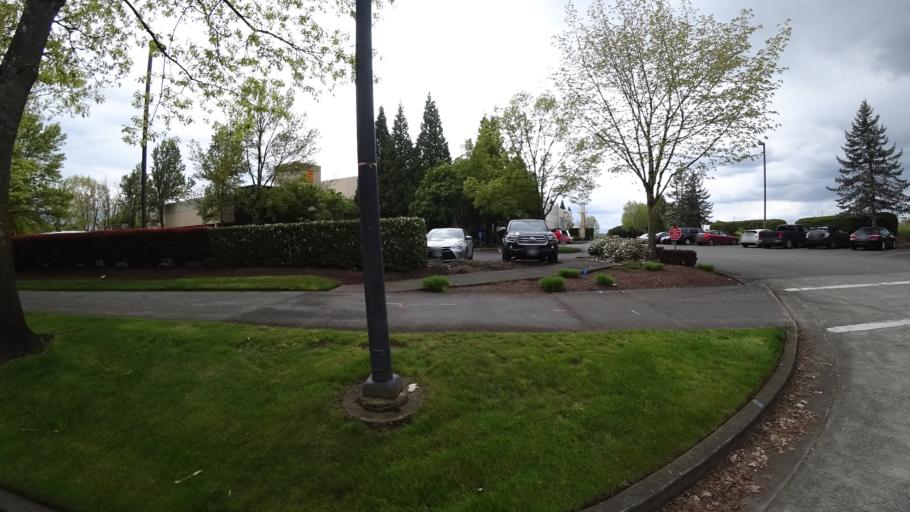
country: US
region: Oregon
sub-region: Washington County
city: Rockcreek
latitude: 45.5471
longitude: -122.9325
